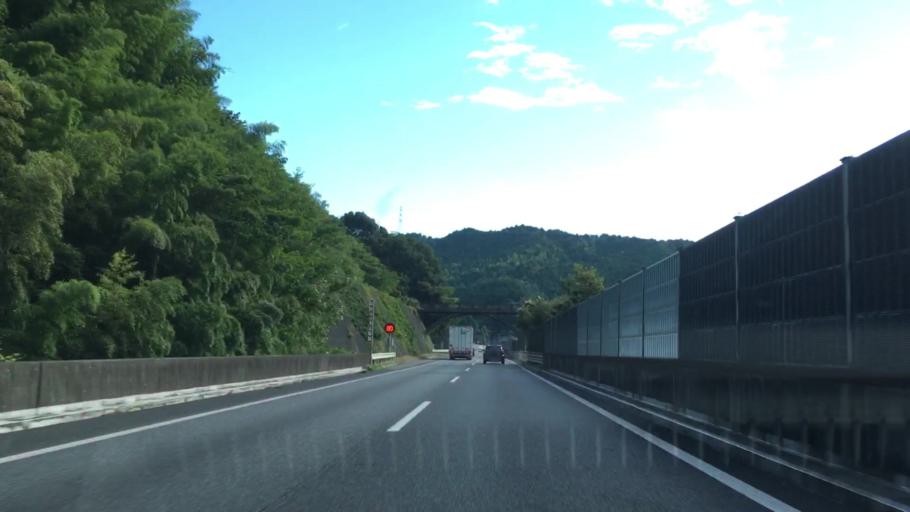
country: JP
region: Yamaguchi
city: Iwakuni
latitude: 34.1603
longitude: 132.1532
